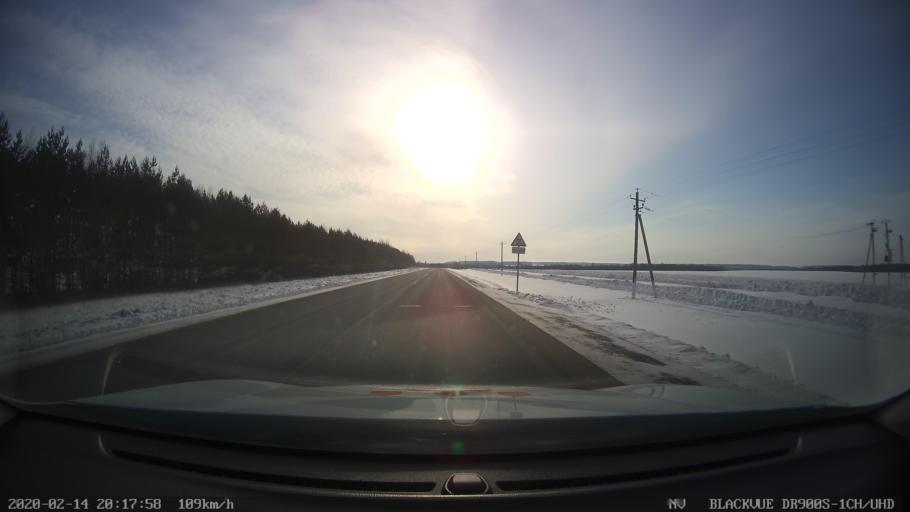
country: RU
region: Tatarstan
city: Verkhniy Uslon
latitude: 55.5928
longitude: 48.8828
